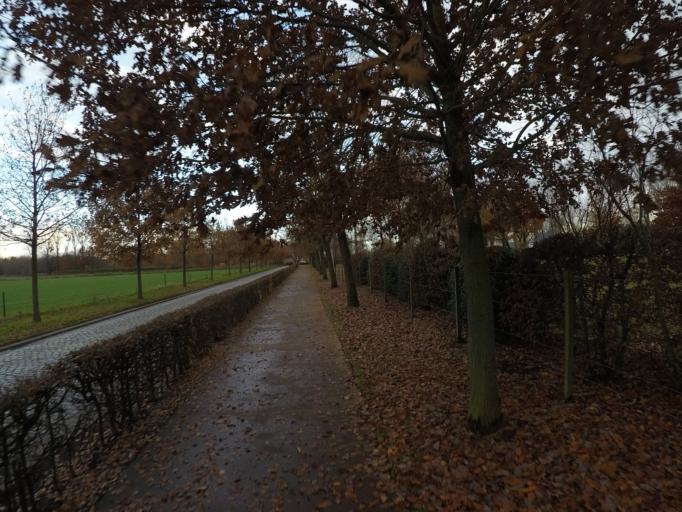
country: BE
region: Flanders
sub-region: Provincie Vlaams-Brabant
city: Londerzeel
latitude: 51.0020
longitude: 4.2685
